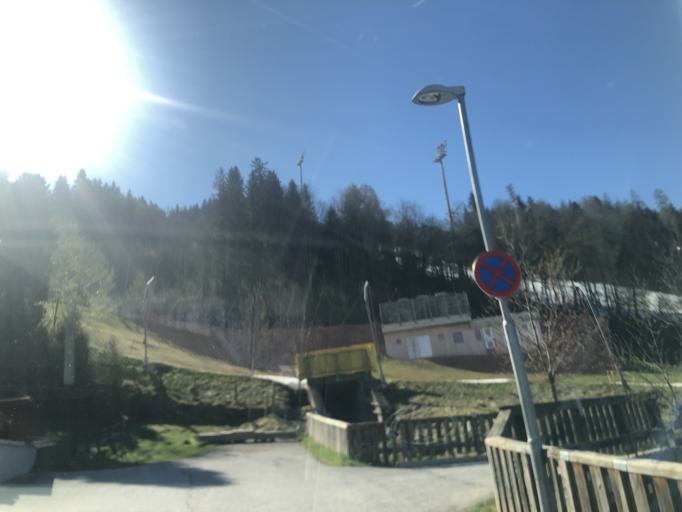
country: AT
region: Styria
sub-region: Politischer Bezirk Liezen
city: Schladming
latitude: 47.3932
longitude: 13.6960
